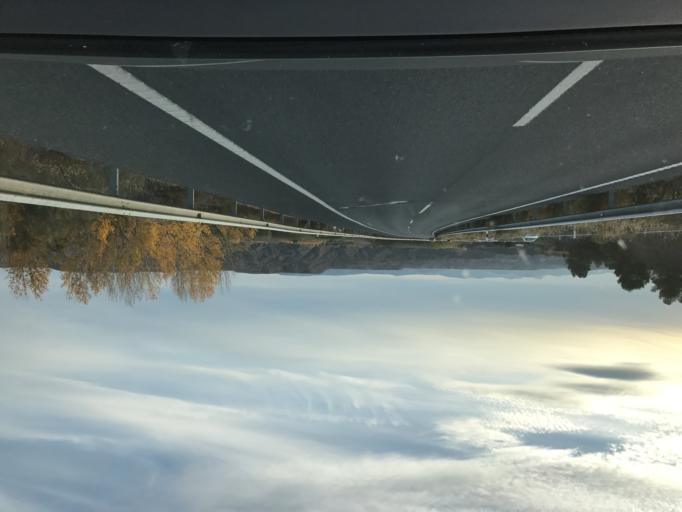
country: ES
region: Andalusia
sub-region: Provincia de Granada
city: Purullena
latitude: 37.3282
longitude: -3.1804
